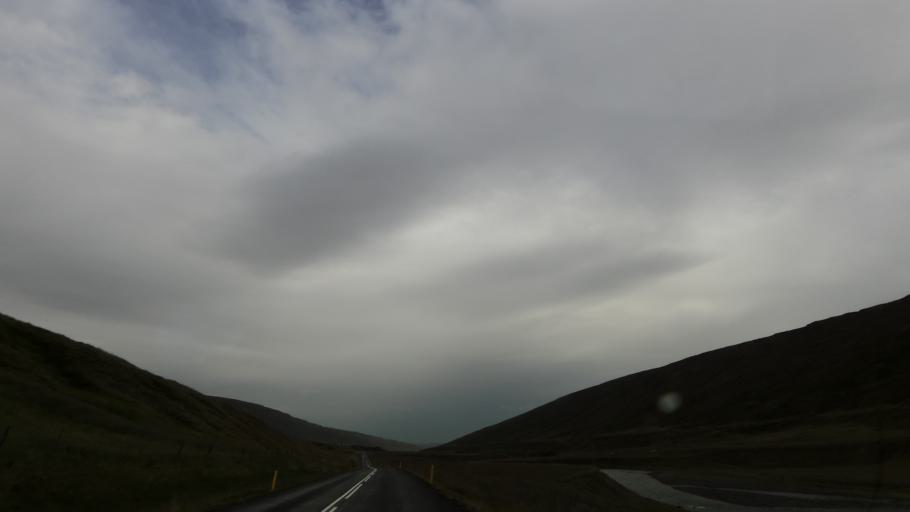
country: IS
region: East
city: Egilsstadir
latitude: 65.3192
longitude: -15.1063
